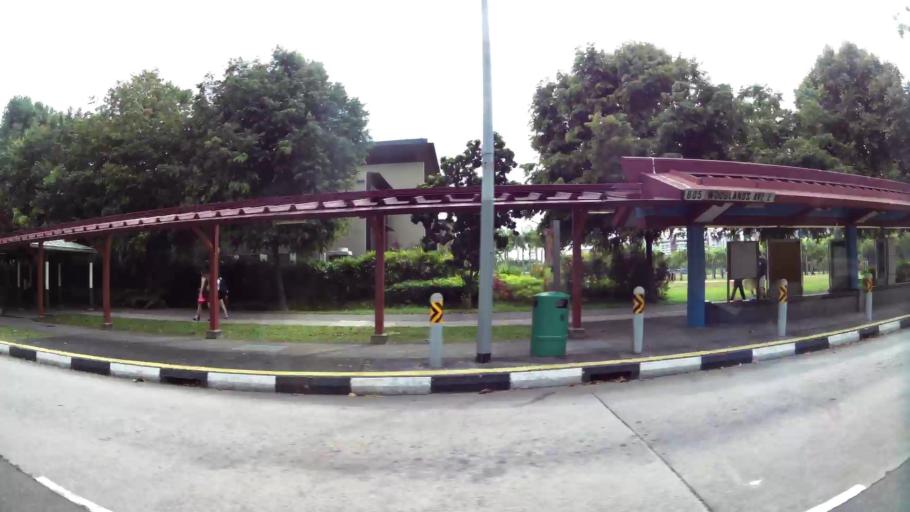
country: MY
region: Johor
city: Johor Bahru
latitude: 1.4404
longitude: 103.7860
